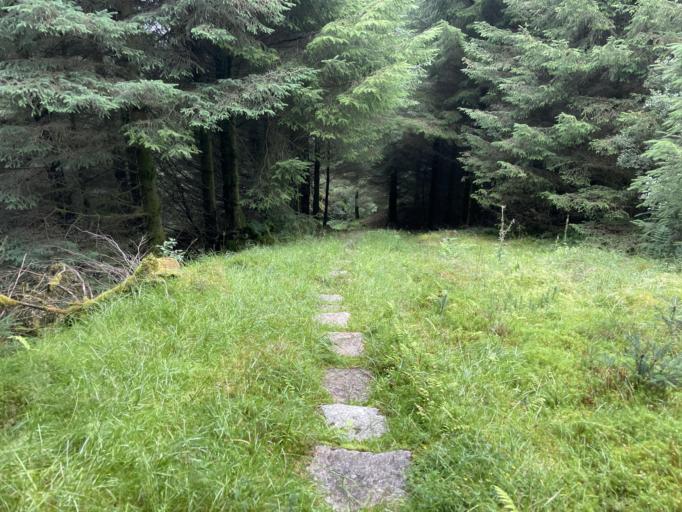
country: GB
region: Scotland
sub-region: South Ayrshire
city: Maybole
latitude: 55.2044
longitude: -4.6737
